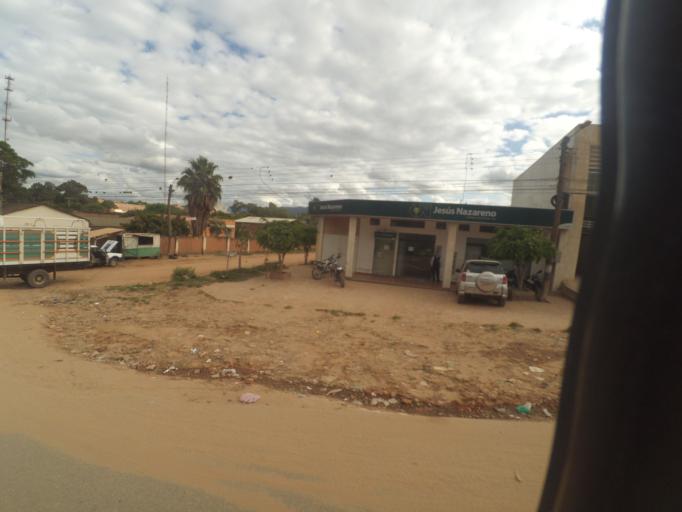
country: BO
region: Santa Cruz
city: Samaipata
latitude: -18.1638
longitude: -63.9245
